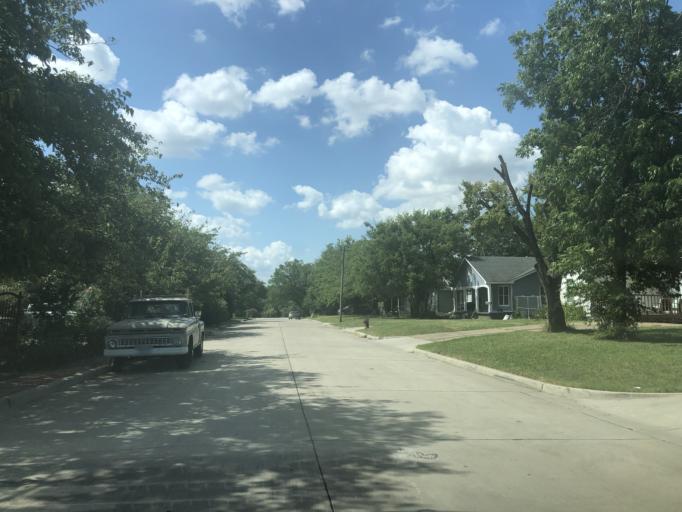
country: US
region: Texas
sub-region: Dallas County
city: Grand Prairie
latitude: 32.7380
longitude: -97.0025
